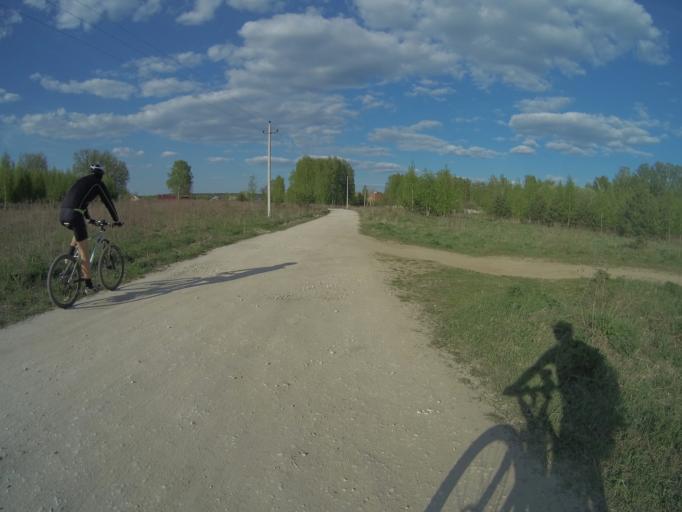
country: RU
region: Vladimir
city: Raduzhnyy
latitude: 55.9989
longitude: 40.2589
